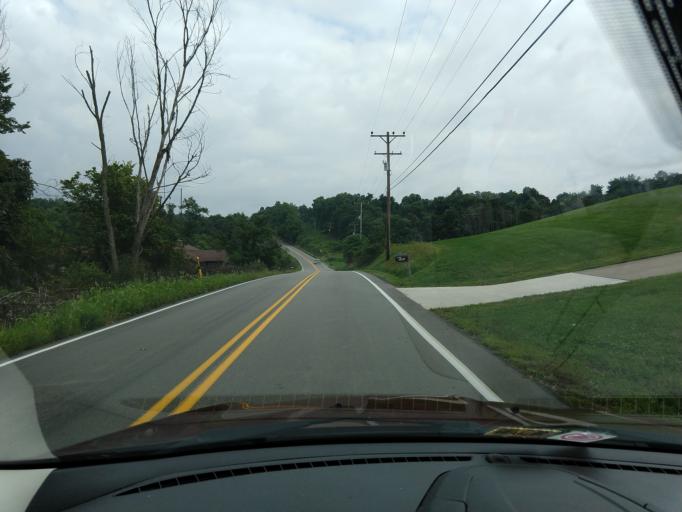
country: US
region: Pennsylvania
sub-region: Washington County
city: Baidland
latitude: 40.1909
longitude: -79.9996
